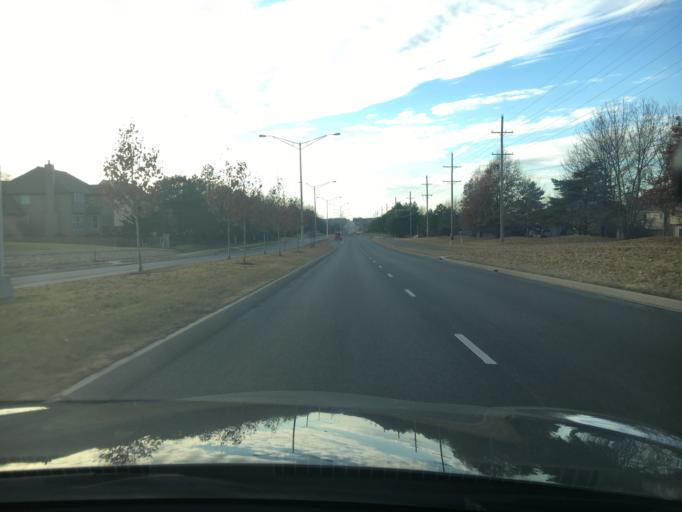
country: US
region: Kansas
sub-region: Johnson County
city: Lenexa
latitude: 38.8693
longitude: -94.6794
